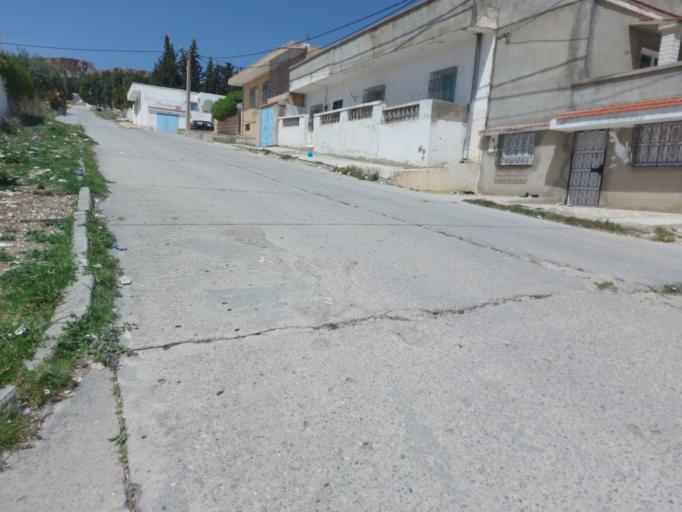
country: TN
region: Kef
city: El Kef
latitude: 36.1814
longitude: 8.7290
